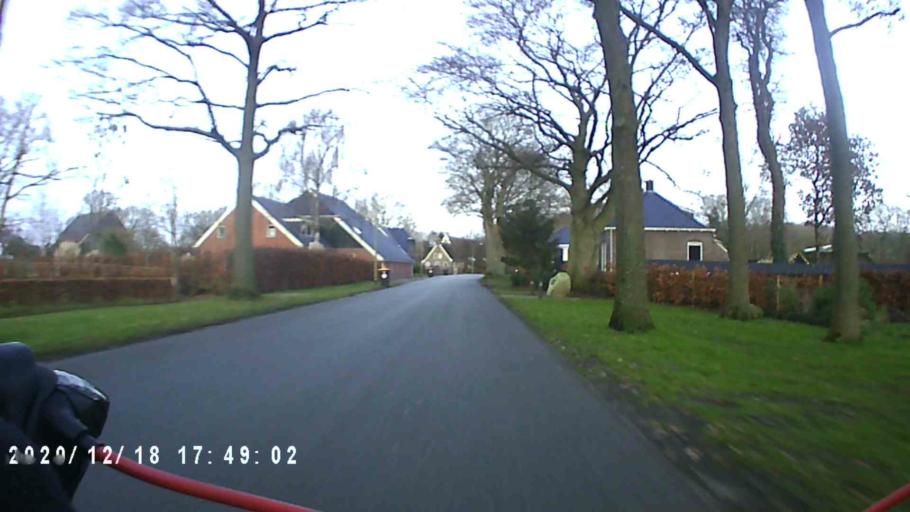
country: NL
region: Drenthe
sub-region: Gemeente Tynaarlo
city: Vries
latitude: 53.1122
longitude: 6.5853
